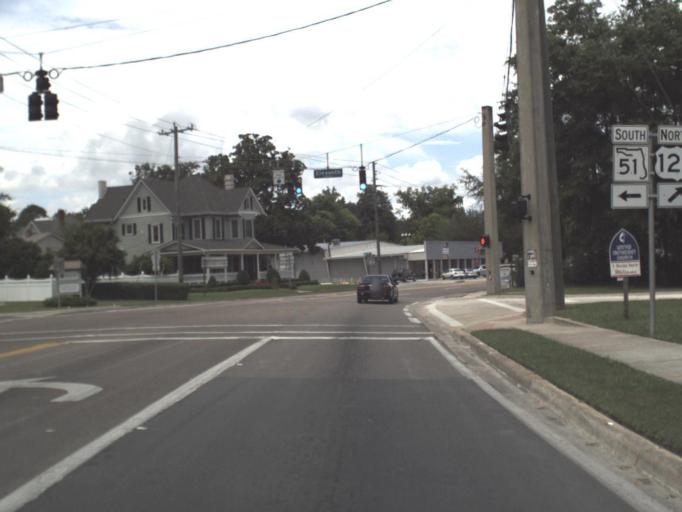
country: US
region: Florida
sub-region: Suwannee County
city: Live Oak
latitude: 30.2898
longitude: -82.9877
